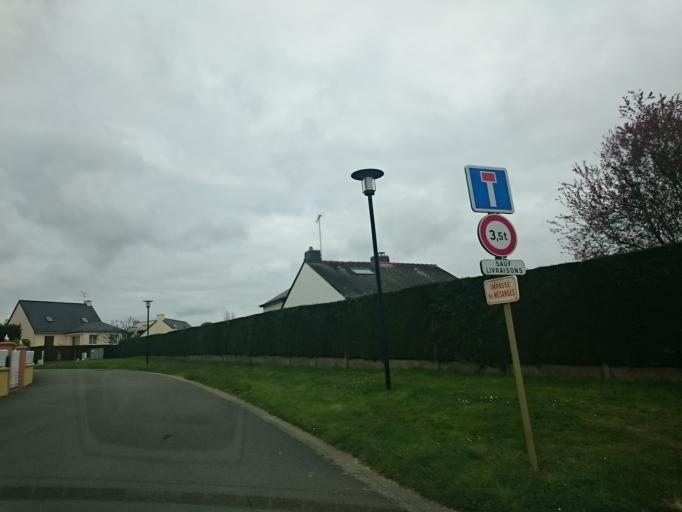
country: FR
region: Brittany
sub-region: Departement d'Ille-et-Vilaine
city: Crevin
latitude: 47.9355
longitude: -1.6556
